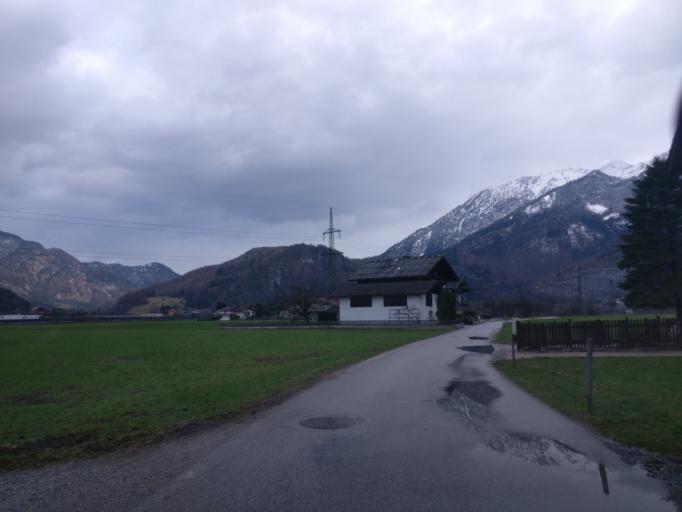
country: AT
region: Salzburg
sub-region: Politischer Bezirk Hallein
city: Golling an der Salzach
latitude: 47.5872
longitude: 13.1686
